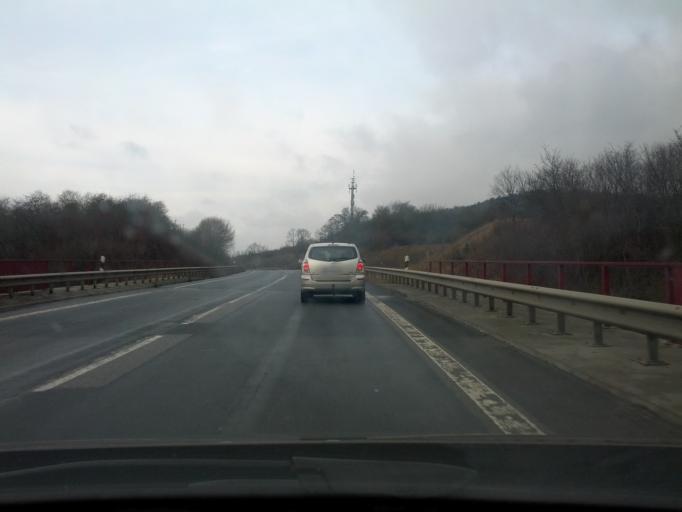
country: DE
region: Lower Saxony
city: Scheden
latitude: 51.3926
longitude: 9.7796
